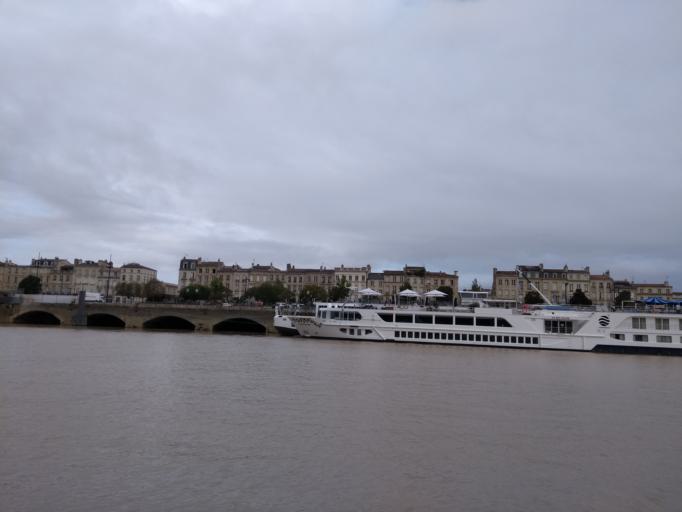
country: FR
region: Aquitaine
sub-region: Departement de la Gironde
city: Bordeaux
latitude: 44.8521
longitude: -0.5654
